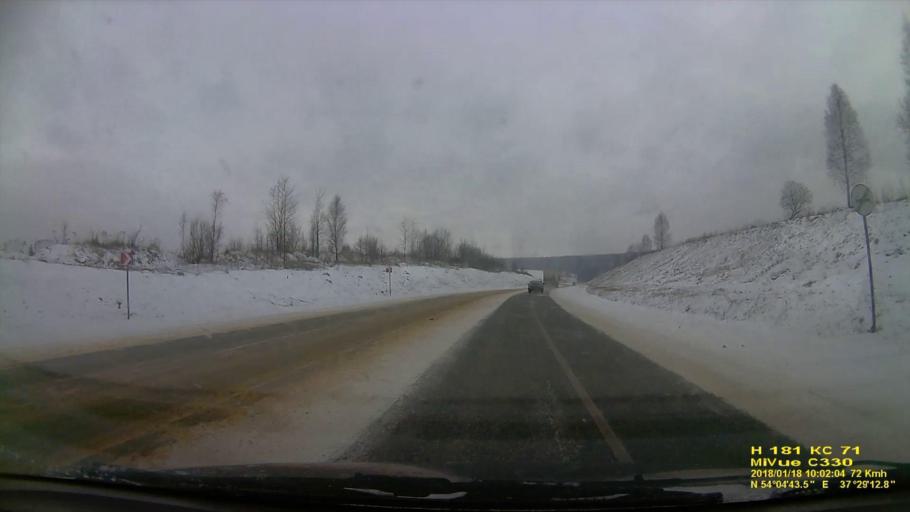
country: RU
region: Tula
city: Pervomayskiy
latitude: 54.0788
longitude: 37.4869
